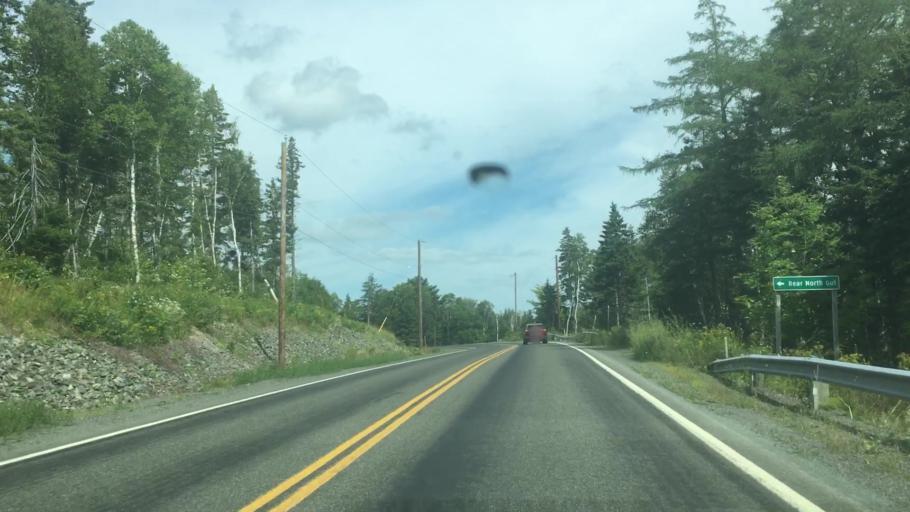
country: CA
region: Nova Scotia
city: Sydney Mines
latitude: 46.2117
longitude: -60.6204
